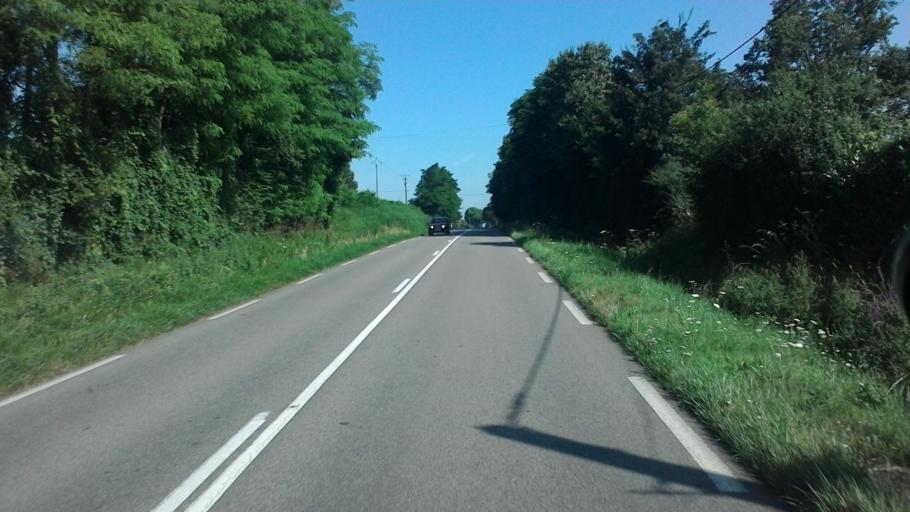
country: FR
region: Rhone-Alpes
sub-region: Departement de l'Ain
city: Saint-Trivier-de-Courtes
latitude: 46.4294
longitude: 5.0966
